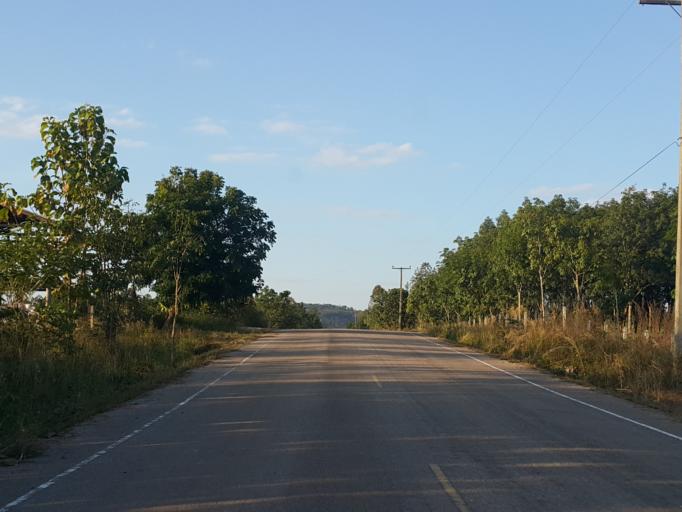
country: TH
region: Lampang
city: Lampang
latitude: 18.4312
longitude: 99.5714
